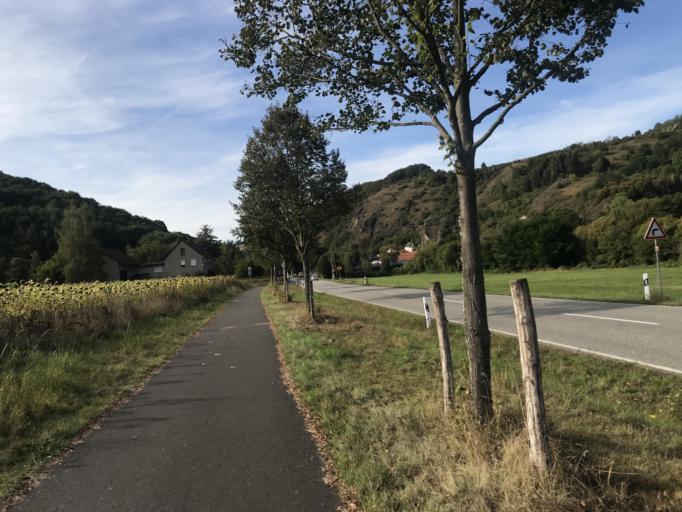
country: DE
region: Rheinland-Pfalz
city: Martinstein
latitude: 49.7999
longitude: 7.5415
